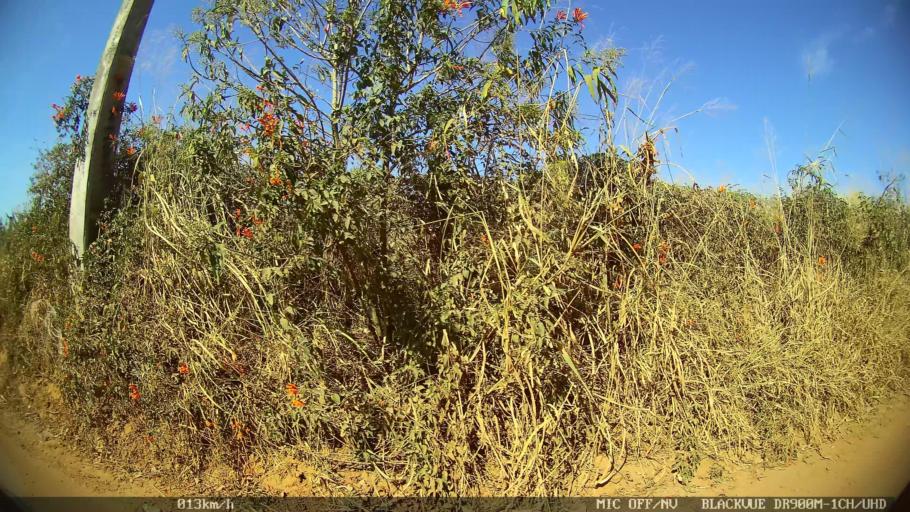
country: BR
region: Sao Paulo
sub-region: Franca
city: Franca
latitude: -20.4589
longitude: -47.4144
